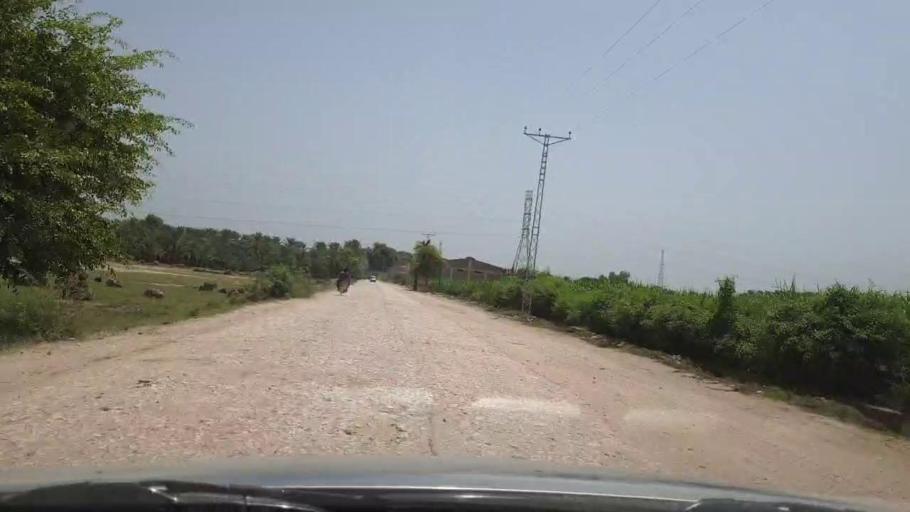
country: PK
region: Sindh
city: Pano Aqil
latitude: 27.8584
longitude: 69.0946
